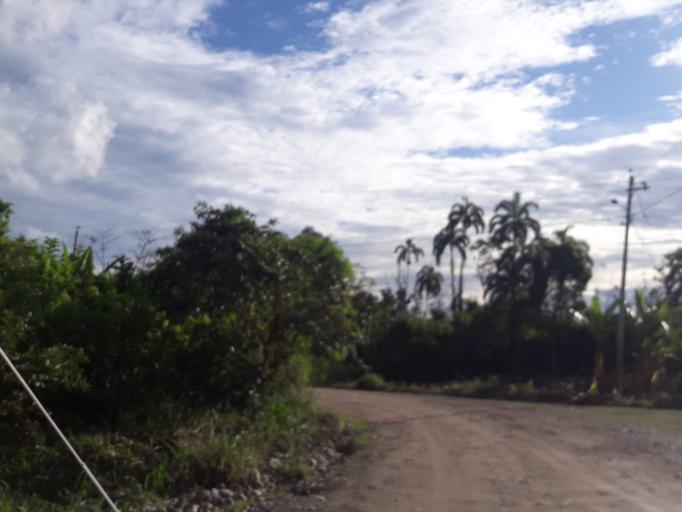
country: EC
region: Orellana
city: Boca Suno
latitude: -0.8837
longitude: -77.2960
